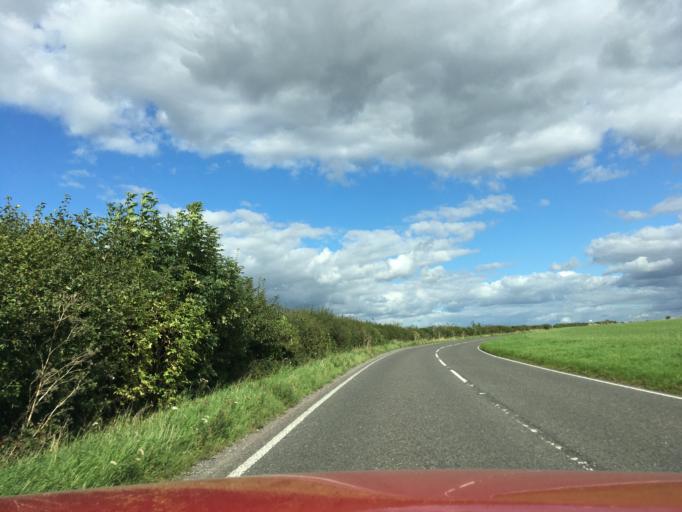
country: GB
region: England
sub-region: Hampshire
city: Abbotts Ann
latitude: 51.1155
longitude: -1.5539
